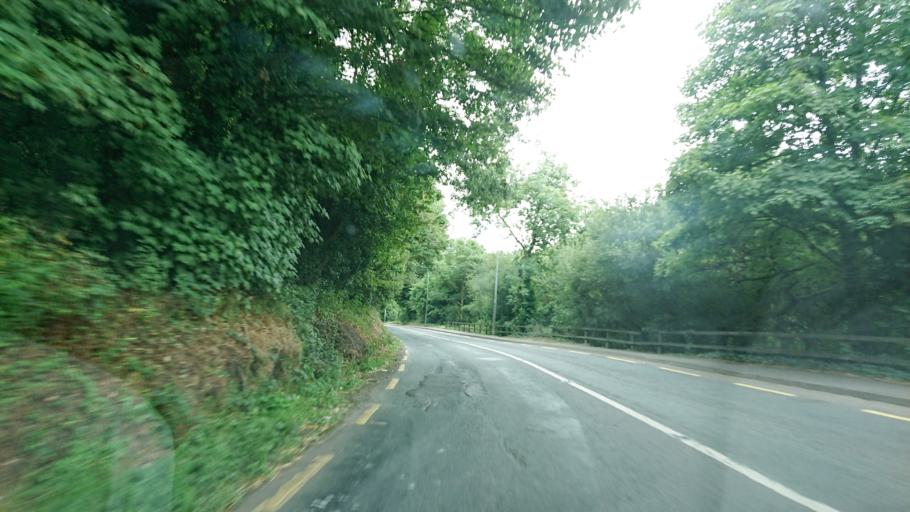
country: IE
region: Munster
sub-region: County Cork
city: Mallow
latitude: 52.1455
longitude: -8.6370
